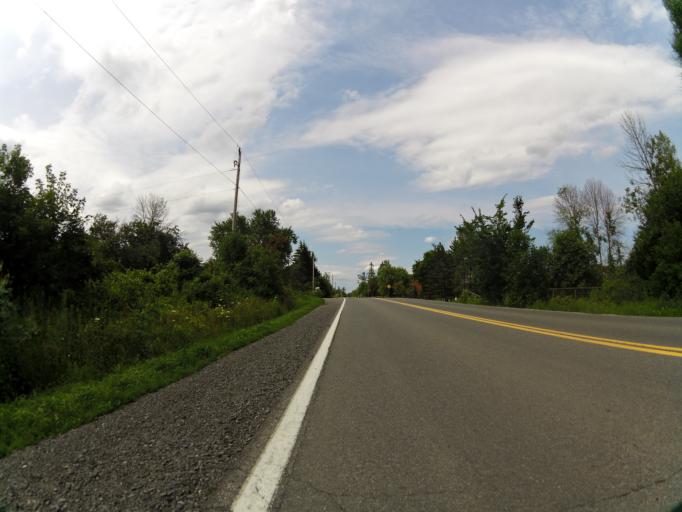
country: CA
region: Ontario
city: Ottawa
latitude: 45.2333
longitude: -75.6104
